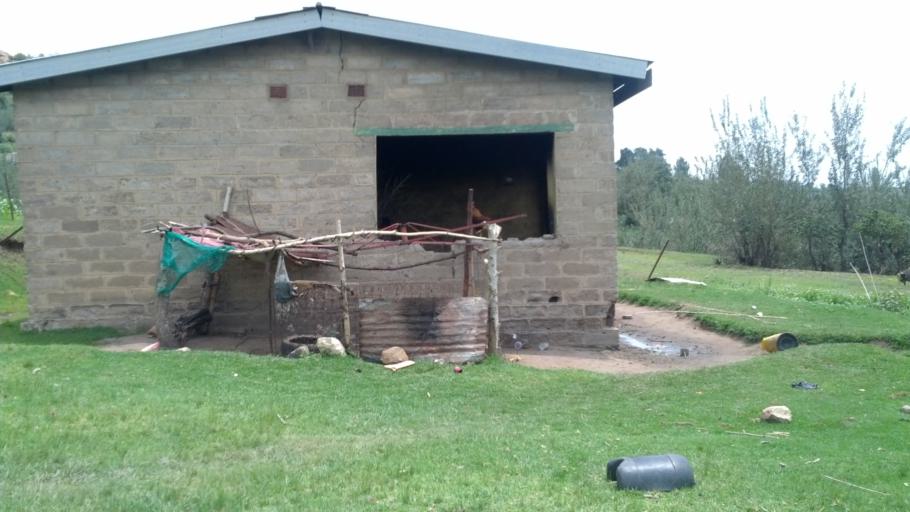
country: LS
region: Leribe
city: Leribe
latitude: -29.0321
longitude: 28.0201
